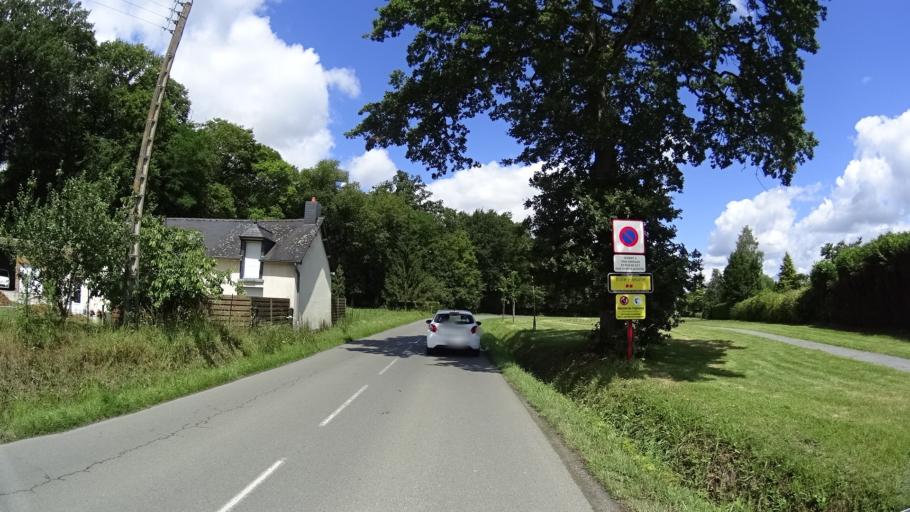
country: FR
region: Brittany
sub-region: Departement d'Ille-et-Vilaine
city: Saint-Gilles
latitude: 48.1483
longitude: -1.8301
